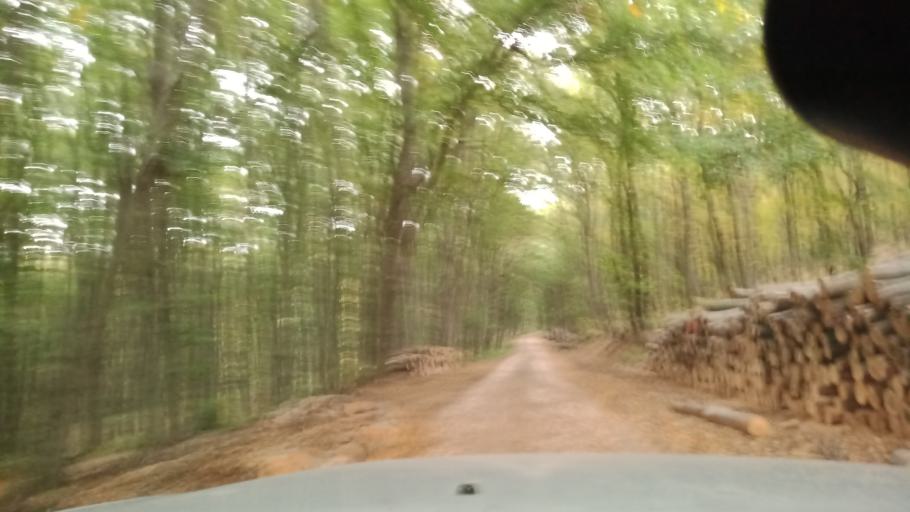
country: HU
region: Fejer
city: Mor
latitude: 47.3808
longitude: 18.2654
